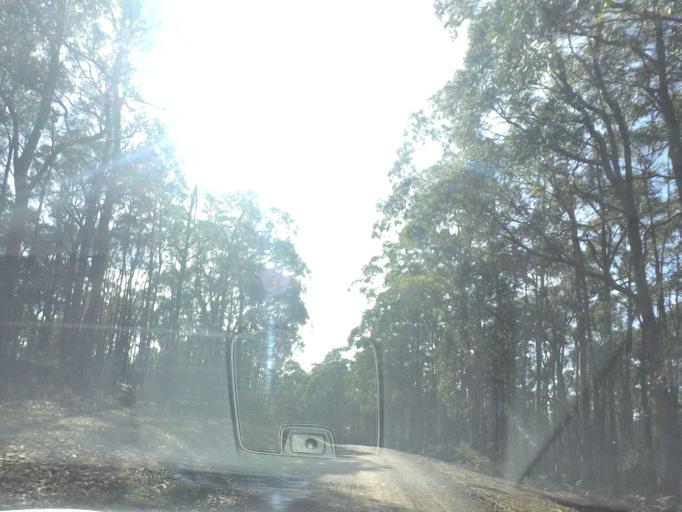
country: AU
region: Victoria
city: Brown Hill
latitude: -37.4372
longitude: 144.2075
